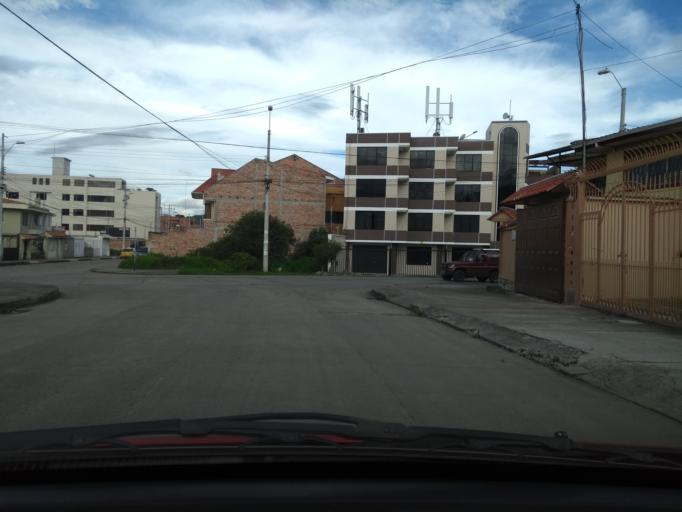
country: EC
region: Azuay
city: Cuenca
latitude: -2.9092
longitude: -79.0240
